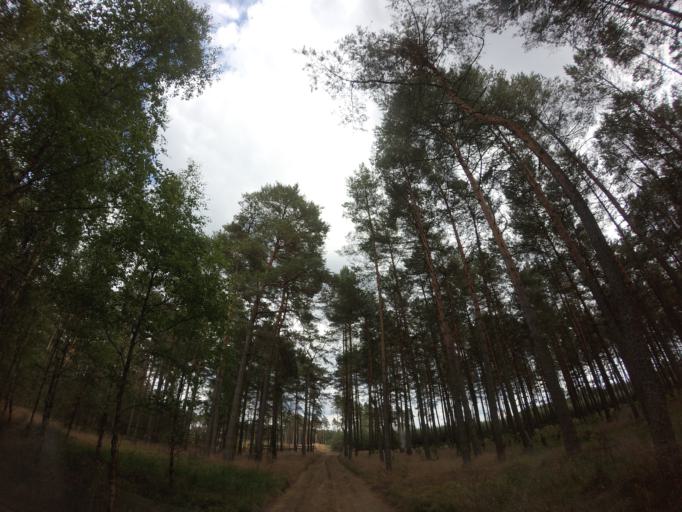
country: PL
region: West Pomeranian Voivodeship
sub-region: Powiat choszczenski
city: Drawno
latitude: 53.1603
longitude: 15.7392
